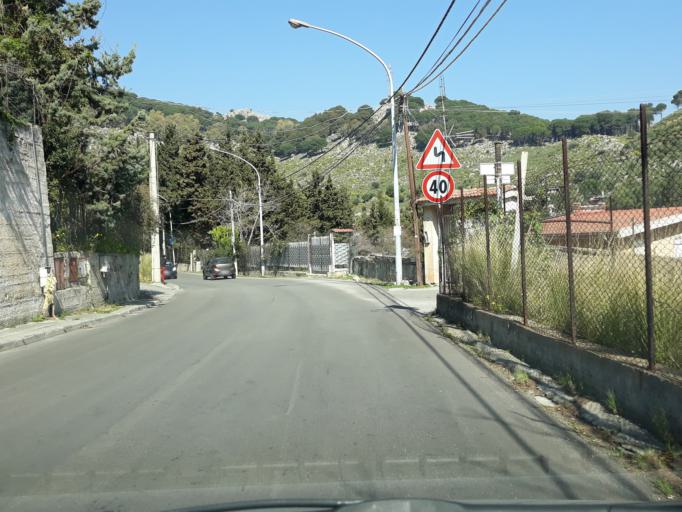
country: IT
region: Sicily
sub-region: Palermo
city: Piano dei Geli
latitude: 38.1160
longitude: 13.2898
